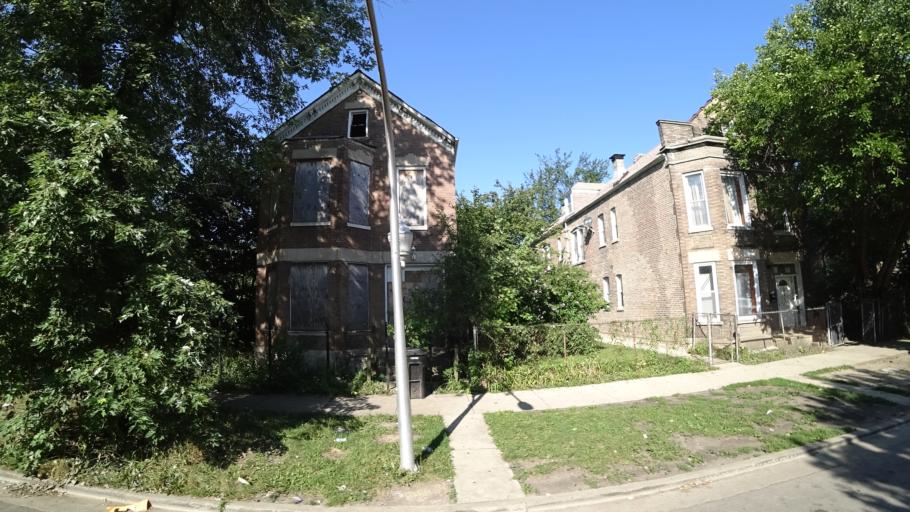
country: US
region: Illinois
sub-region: Cook County
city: Cicero
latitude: 41.8612
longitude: -87.7226
